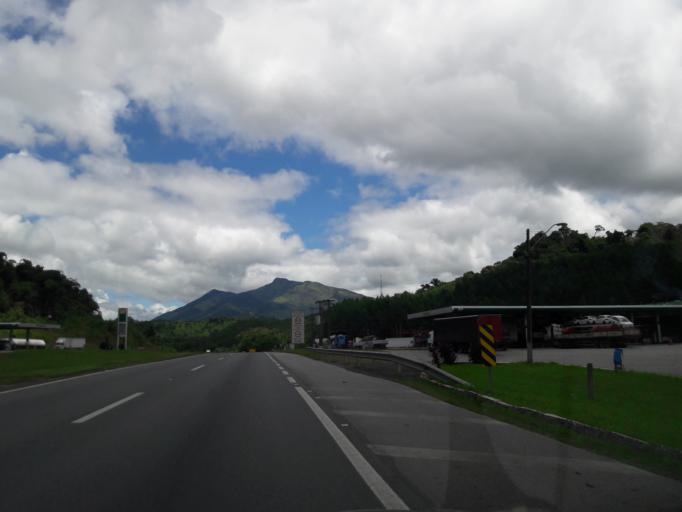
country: BR
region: Parana
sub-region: Antonina
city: Antonina
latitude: -25.1086
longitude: -48.7452
